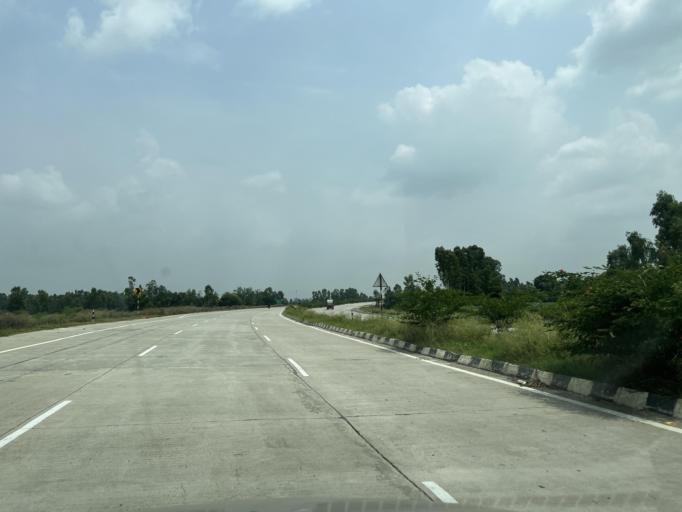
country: IN
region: Uttar Pradesh
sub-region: Bijnor
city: Nagina
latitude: 29.4310
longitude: 78.4120
